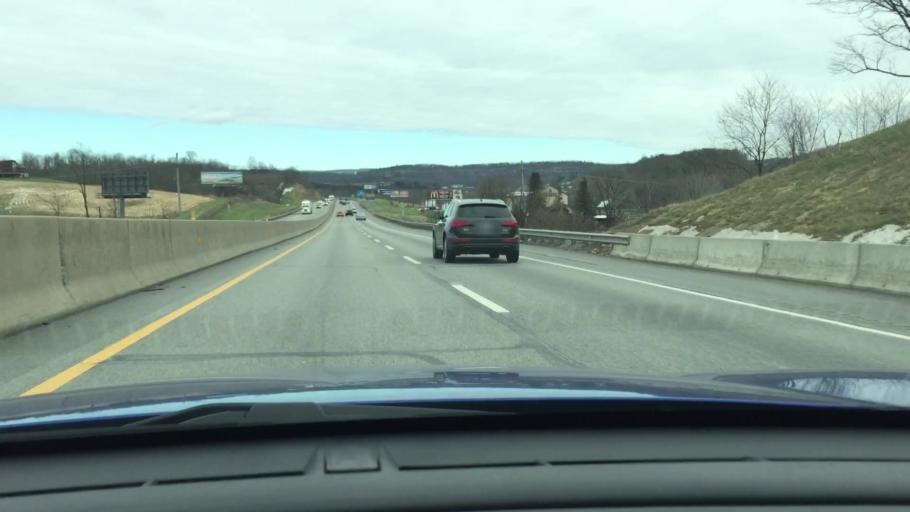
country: US
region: Pennsylvania
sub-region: Bedford County
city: Bedford
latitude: 40.0482
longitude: -78.5526
